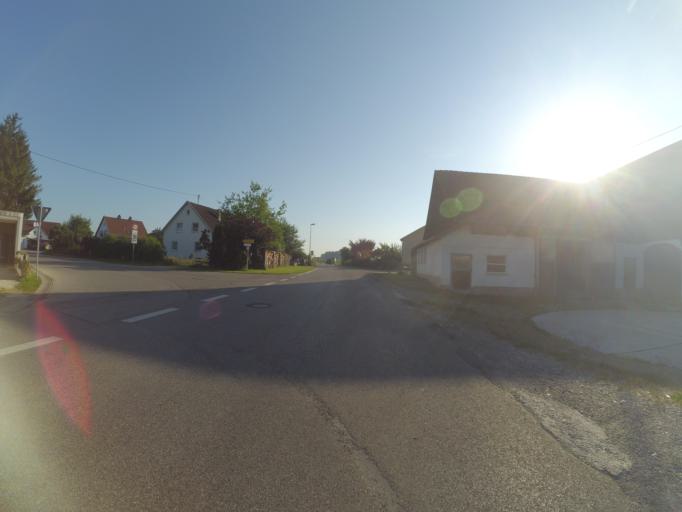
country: DE
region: Bavaria
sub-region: Swabia
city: Dirlewang
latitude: 48.0064
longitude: 10.5372
